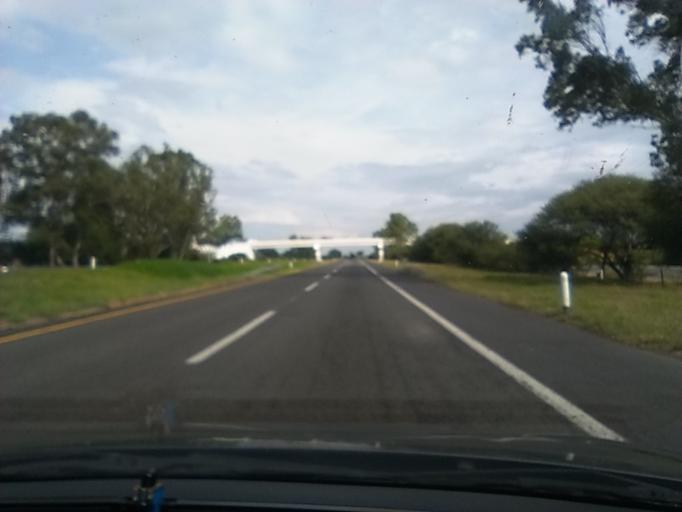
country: MX
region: Jalisco
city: La Barca
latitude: 20.3361
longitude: -102.5974
